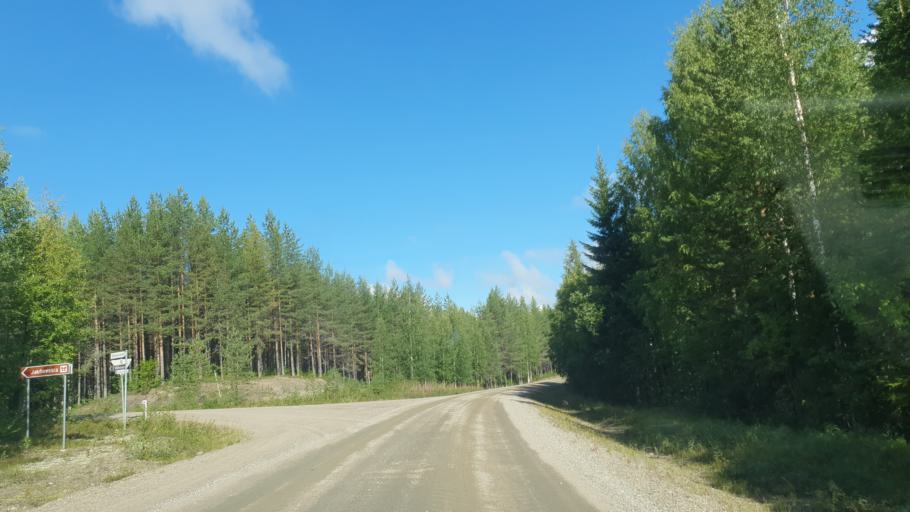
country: FI
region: Kainuu
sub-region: Kehys-Kainuu
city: Kuhmo
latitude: 64.0328
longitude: 29.1722
